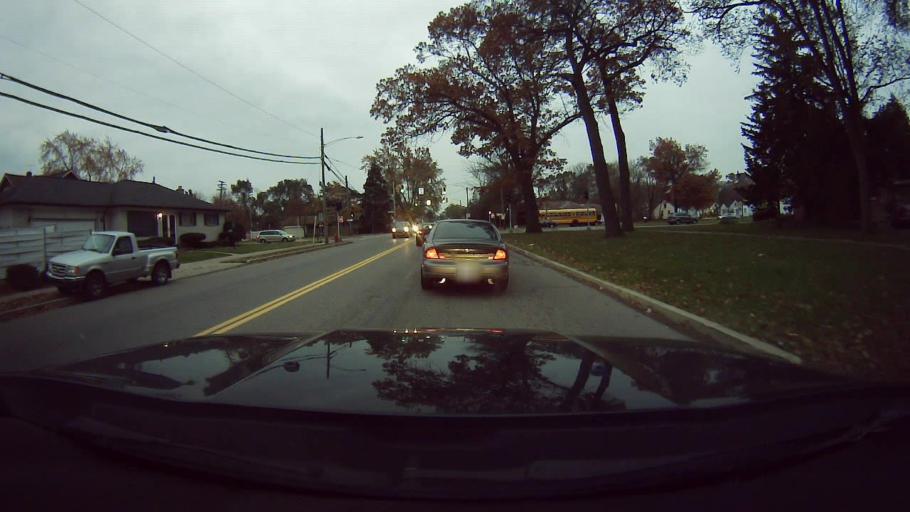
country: US
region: Michigan
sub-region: Oakland County
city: Hazel Park
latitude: 42.4395
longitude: -83.0636
